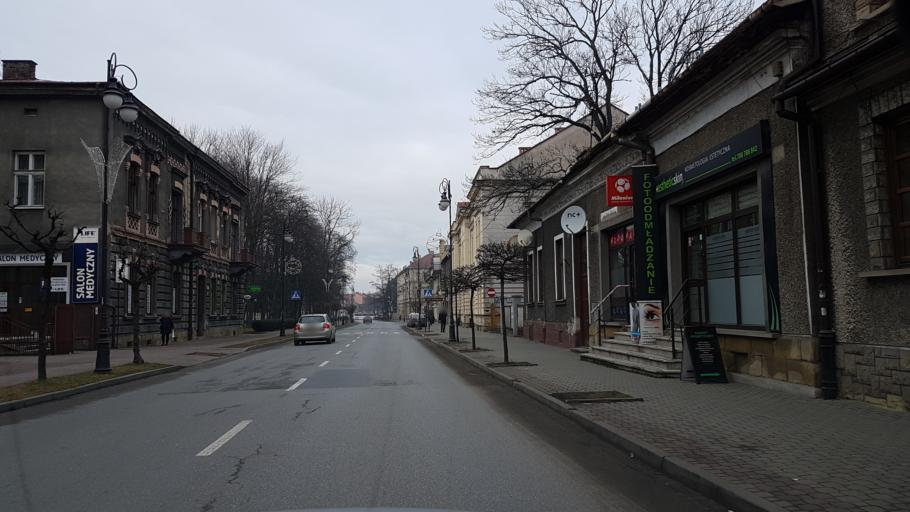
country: PL
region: Lesser Poland Voivodeship
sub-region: Powiat nowosadecki
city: Nowy Sacz
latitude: 49.6198
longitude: 20.6964
